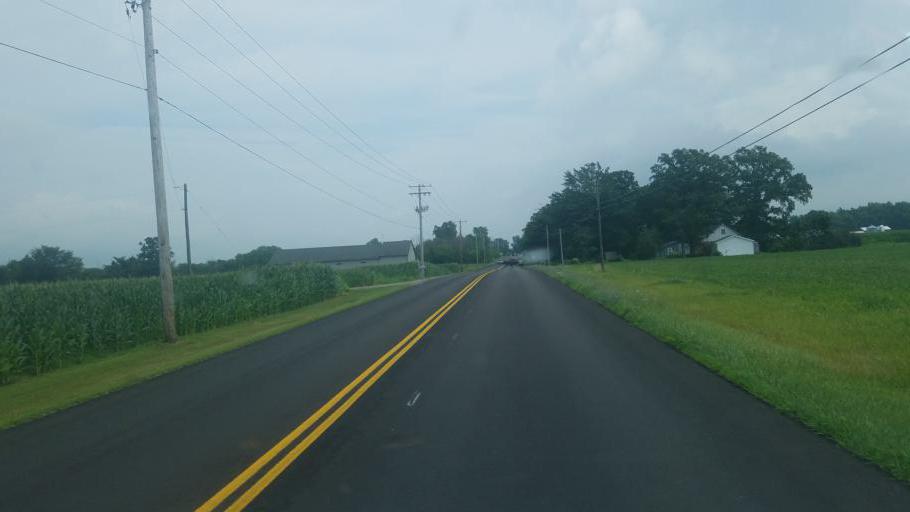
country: US
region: Ohio
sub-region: Logan County
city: Russells Point
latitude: 40.4709
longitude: -83.8480
